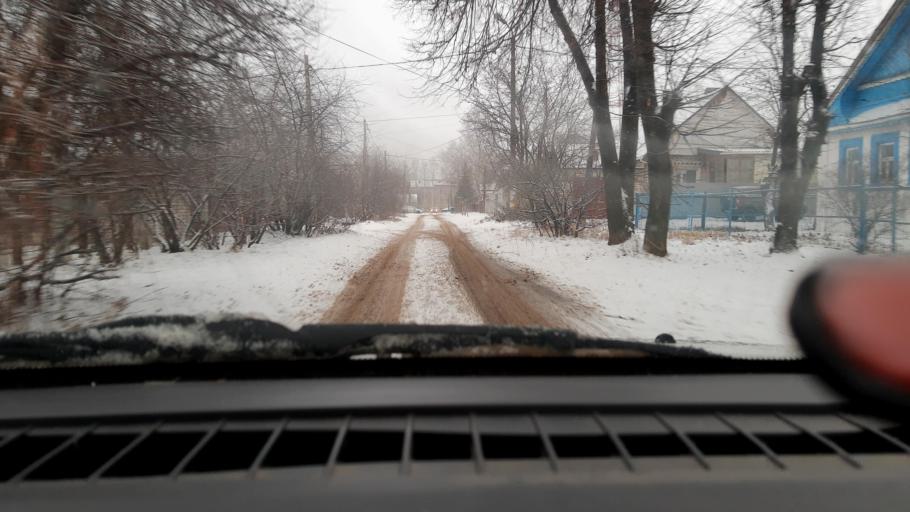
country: RU
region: Nizjnij Novgorod
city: Kstovo
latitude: 56.1401
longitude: 44.2000
